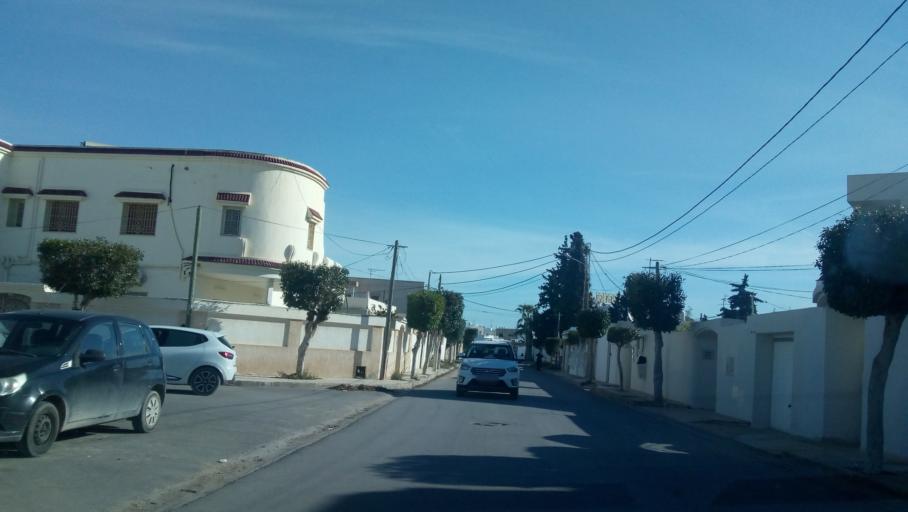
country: TN
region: Safaqis
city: Sfax
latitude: 34.7488
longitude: 10.7395
